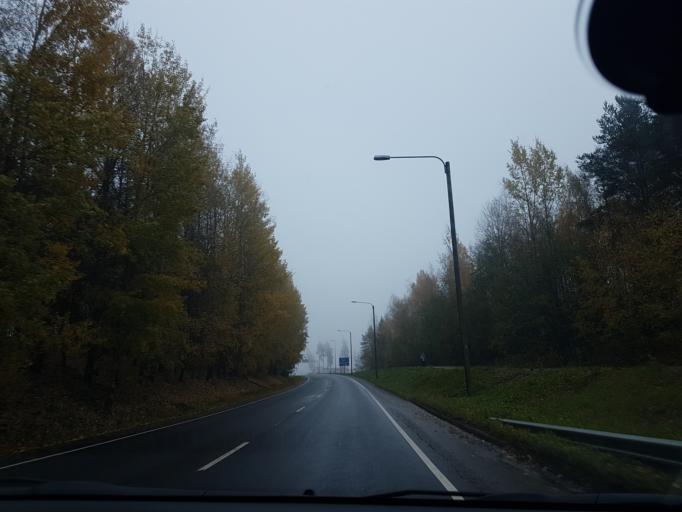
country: FI
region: Uusimaa
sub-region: Helsinki
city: Jaervenpaeae
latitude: 60.4558
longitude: 25.1026
